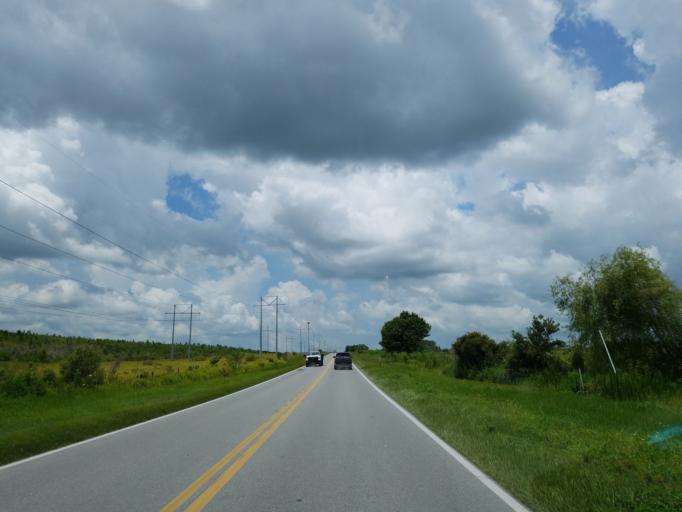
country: US
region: Florida
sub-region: Polk County
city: Fuller Heights
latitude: 27.8508
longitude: -82.0220
